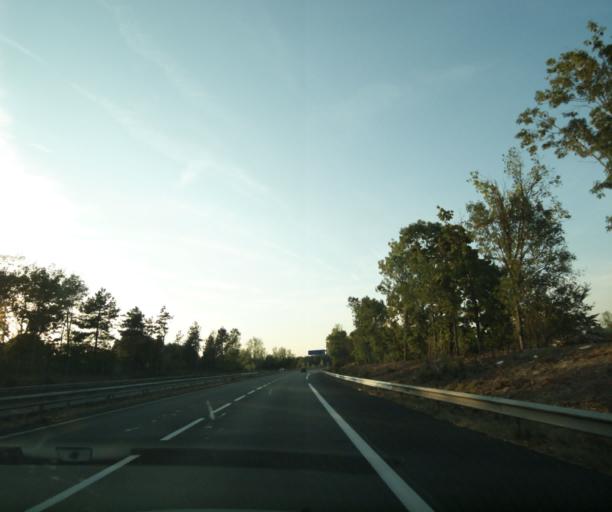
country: FR
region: Aquitaine
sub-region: Departement du Lot-et-Garonne
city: Estillac
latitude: 44.1666
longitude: 0.5839
